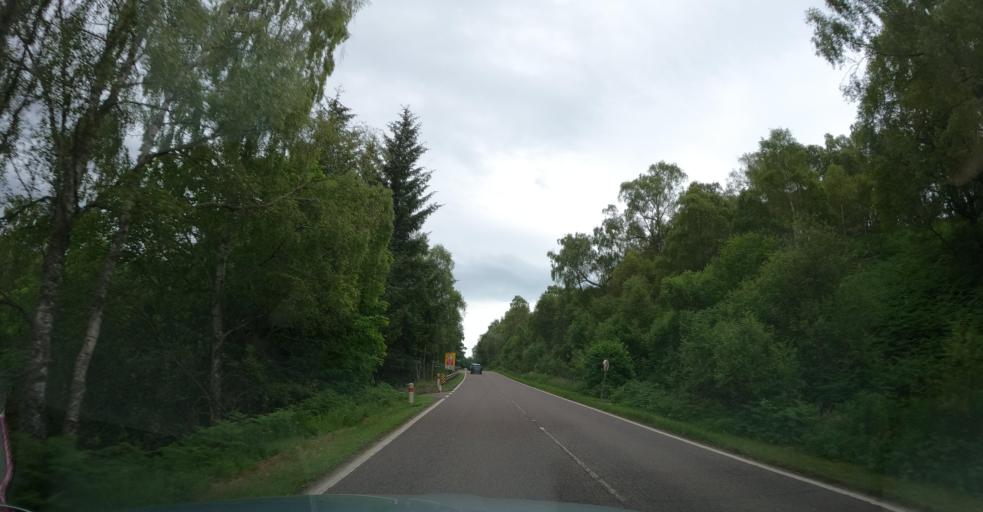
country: GB
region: Scotland
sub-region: Highland
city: Muir of Ord
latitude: 57.5931
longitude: -4.6483
